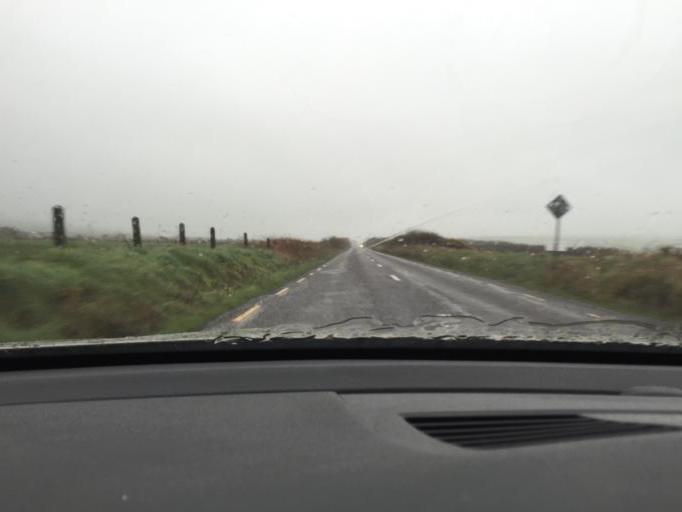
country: IE
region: Munster
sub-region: Ciarrai
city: Dingle
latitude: 52.1406
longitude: -10.1877
